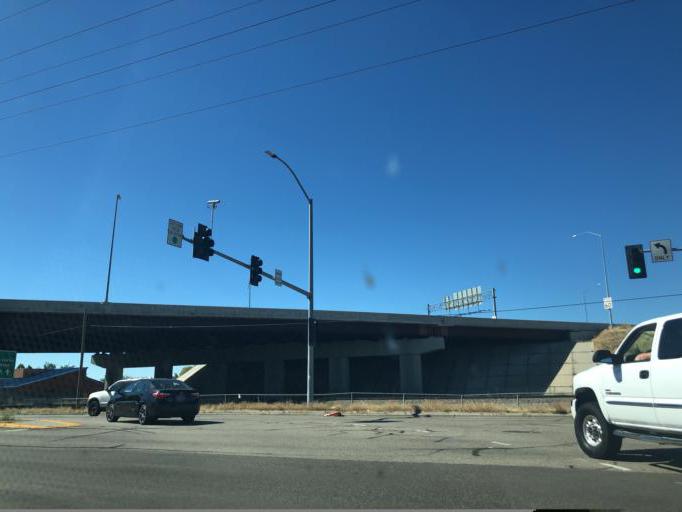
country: US
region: Idaho
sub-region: Ada County
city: Garden City
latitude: 43.6047
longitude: -116.2770
